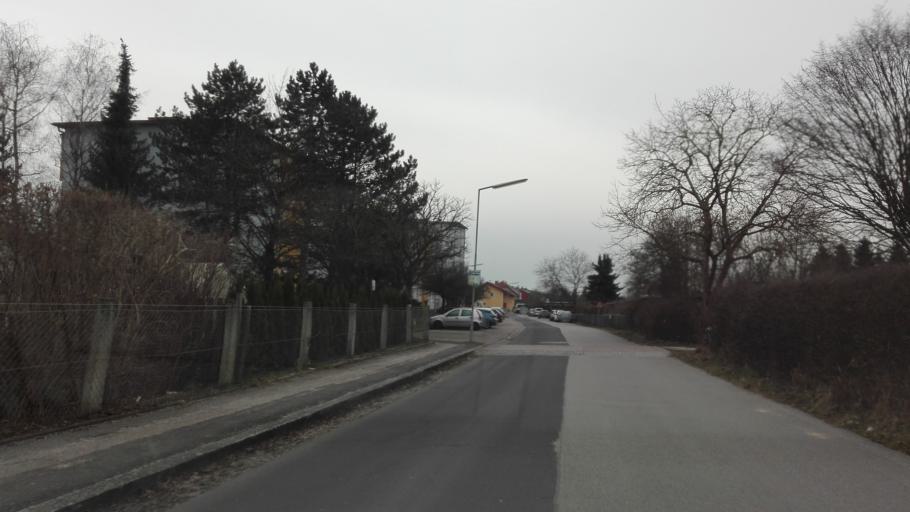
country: AT
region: Upper Austria
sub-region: Politischer Bezirk Linz-Land
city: Traun
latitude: 48.2469
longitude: 14.2566
